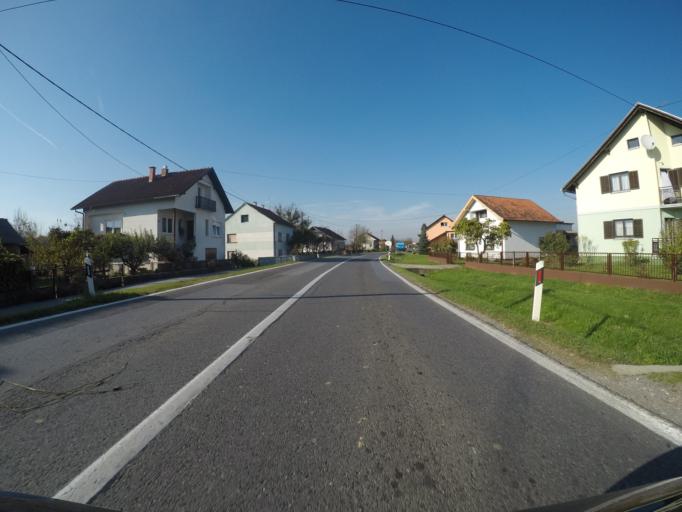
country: HR
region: Bjelovarsko-Bilogorska
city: Predavac
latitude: 45.9225
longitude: 16.7890
